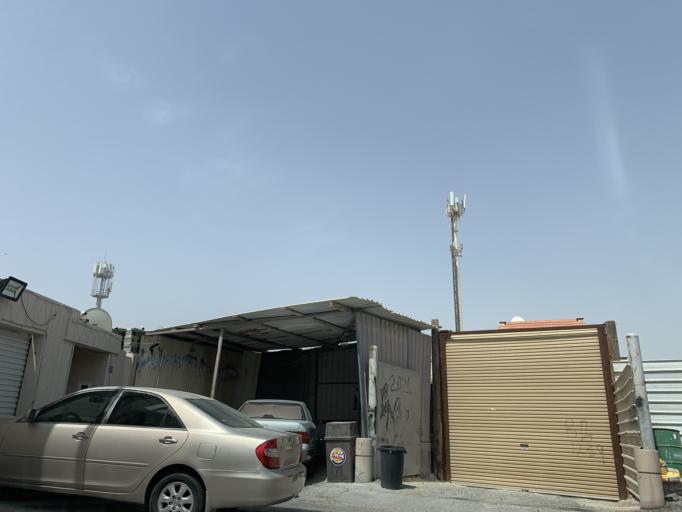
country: BH
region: Northern
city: Madinat `Isa
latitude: 26.1725
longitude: 50.5240
